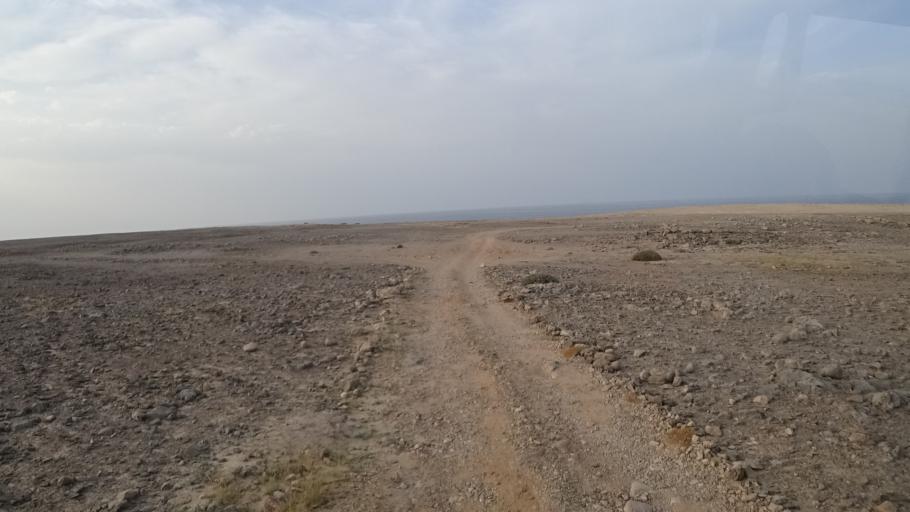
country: OM
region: Ash Sharqiyah
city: Sur
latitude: 22.4567
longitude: 59.8258
